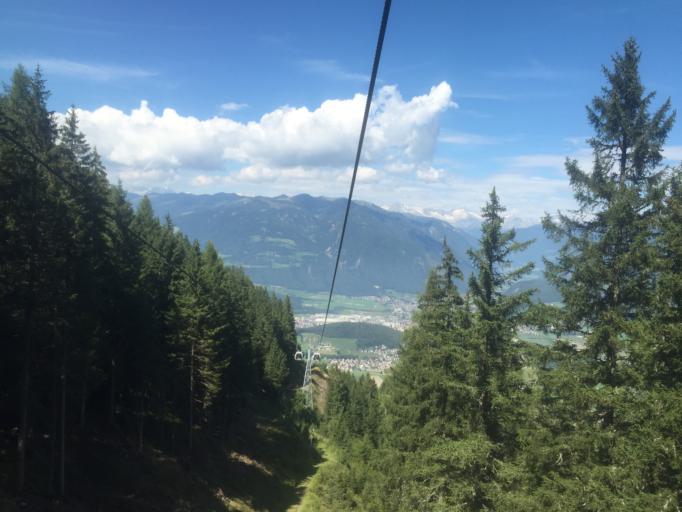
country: IT
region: Trentino-Alto Adige
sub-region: Bolzano
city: Riscone
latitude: 46.7534
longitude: 11.9499
